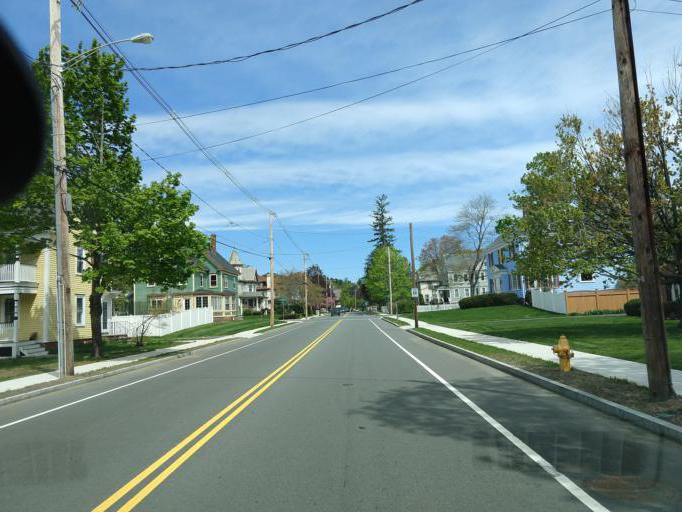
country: US
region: Massachusetts
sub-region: Essex County
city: Amesbury
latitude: 42.8482
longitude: -70.9372
